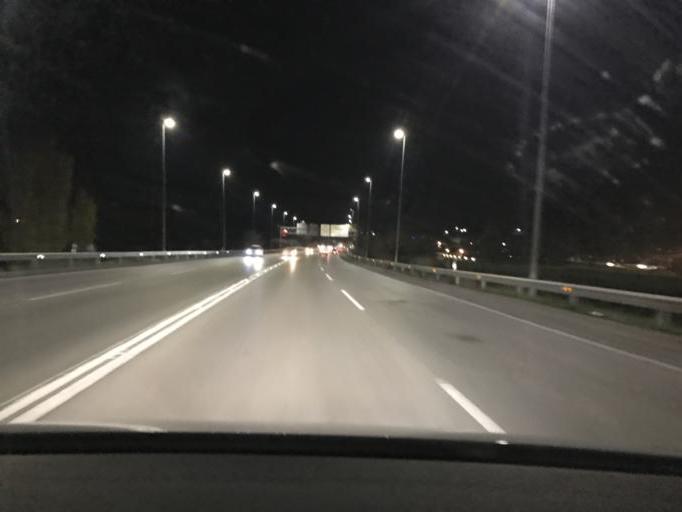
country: ES
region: Andalusia
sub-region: Provincia de Jaen
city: Jaen
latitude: 37.7896
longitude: -3.7763
